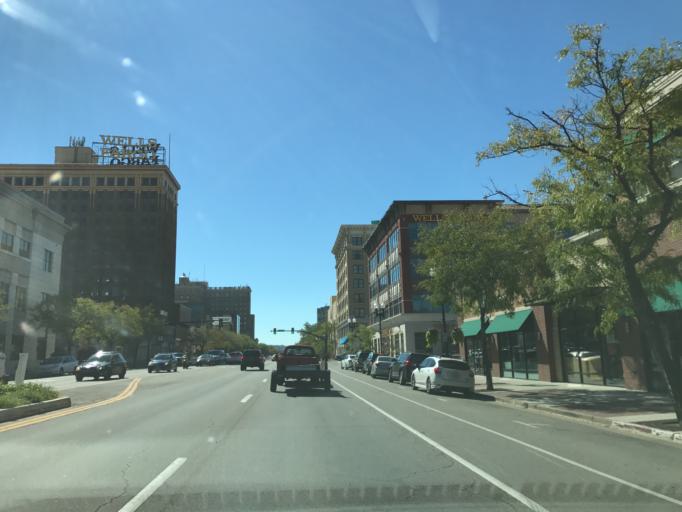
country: US
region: Utah
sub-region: Weber County
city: Ogden
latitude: 41.2238
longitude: -111.9705
